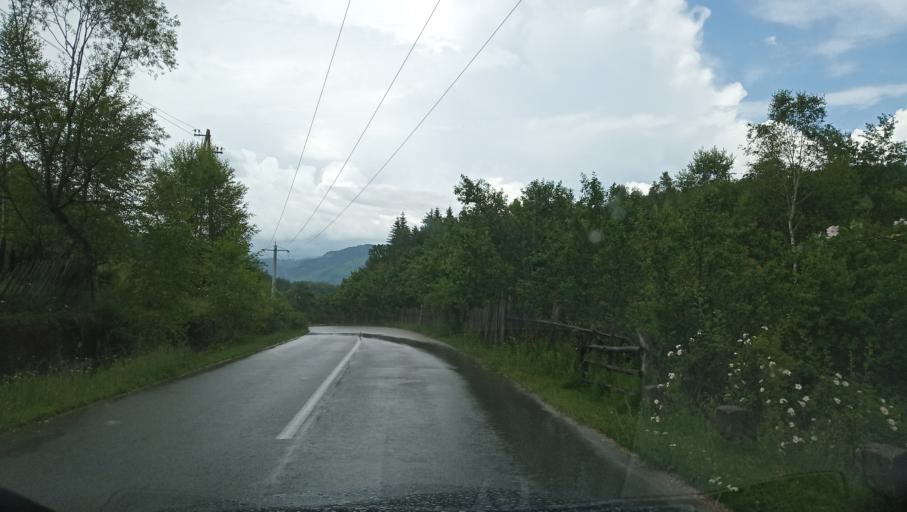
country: RO
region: Hunedoara
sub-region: Oras Petrila
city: Petrila
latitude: 45.4014
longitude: 23.4154
